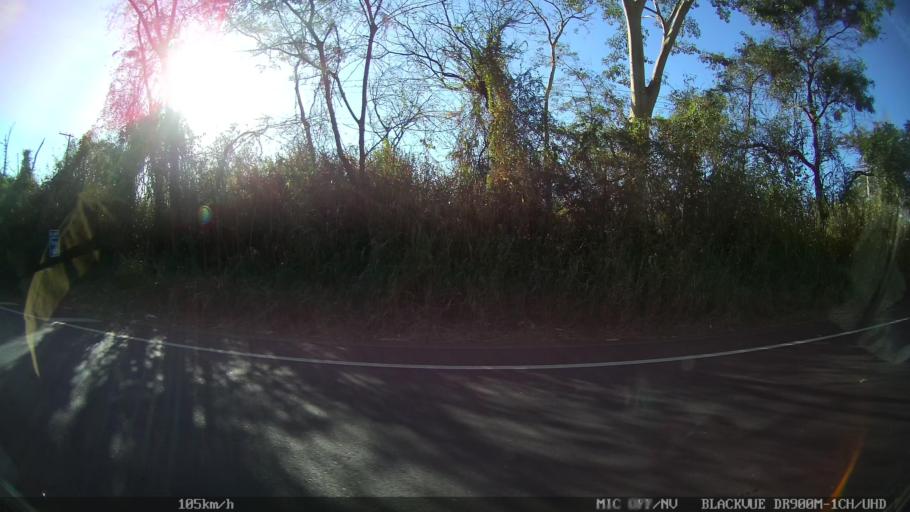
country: BR
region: Sao Paulo
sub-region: Olimpia
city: Olimpia
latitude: -20.7296
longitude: -49.0515
